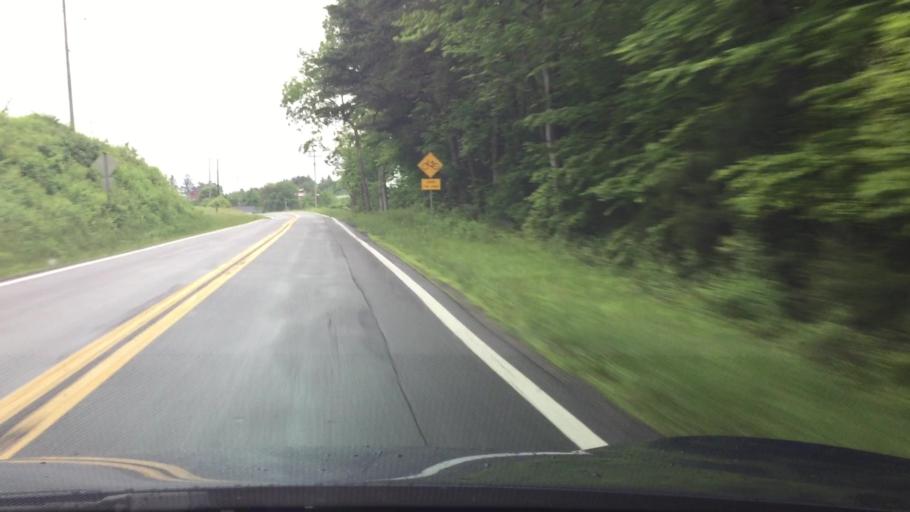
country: US
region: West Virginia
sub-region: Summers County
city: Hinton
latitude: 37.5745
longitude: -80.7877
